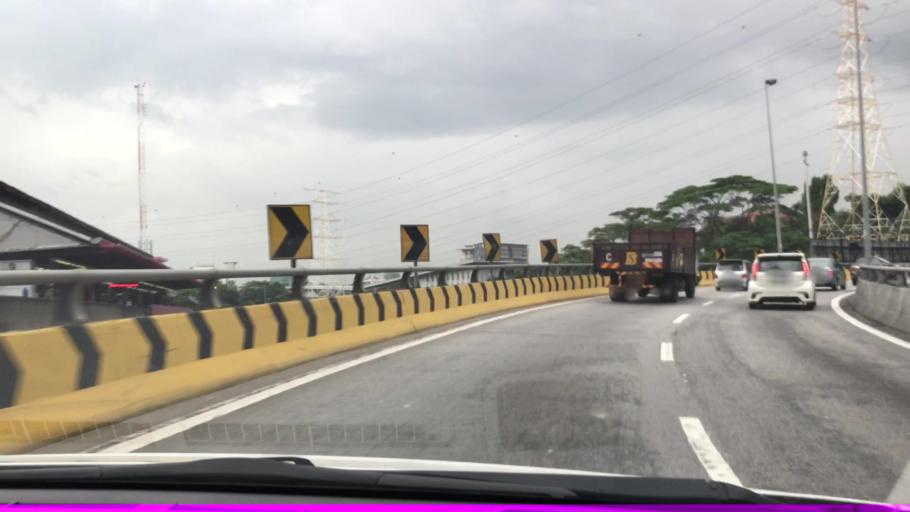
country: MY
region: Kuala Lumpur
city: Kuala Lumpur
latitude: 3.1148
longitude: 101.6625
